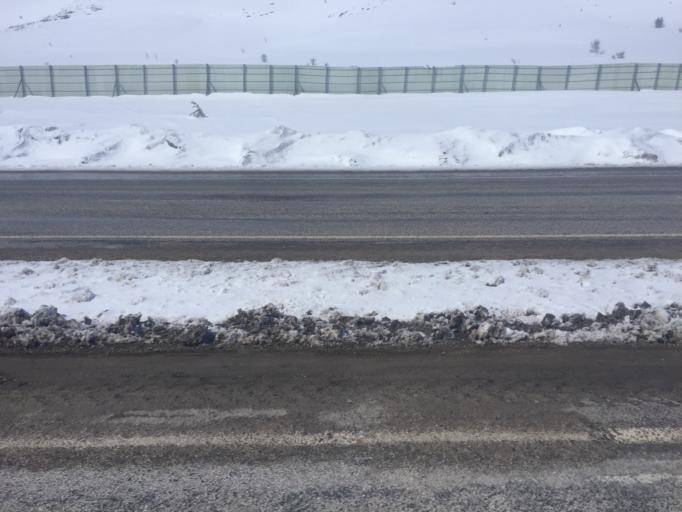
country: TR
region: Kahramanmaras
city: Goksun
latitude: 38.1877
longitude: 36.4567
